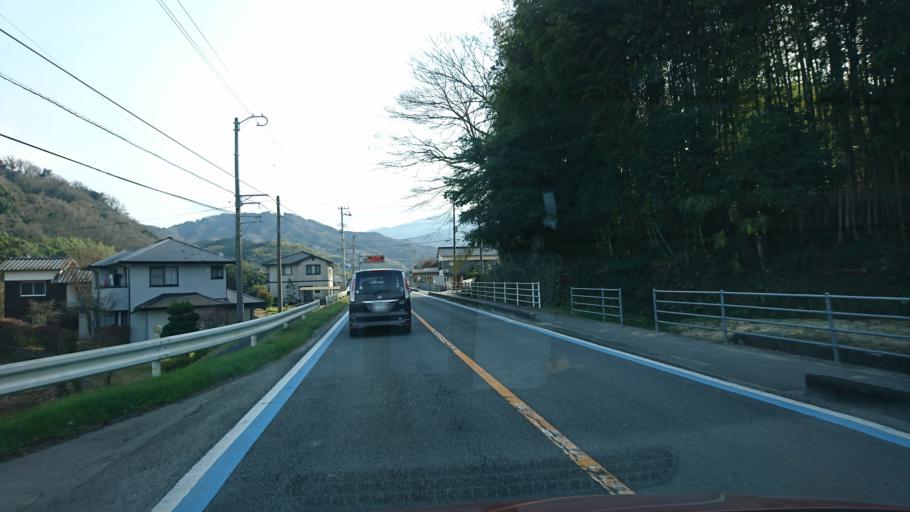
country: JP
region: Ehime
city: Hojo
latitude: 34.0085
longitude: 132.9380
